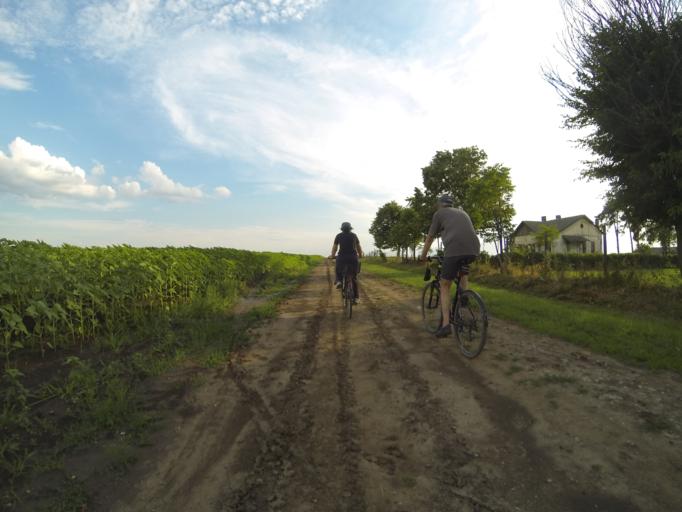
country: RO
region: Dolj
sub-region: Comuna Caloparu
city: Salcuta
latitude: 44.1431
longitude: 23.6945
